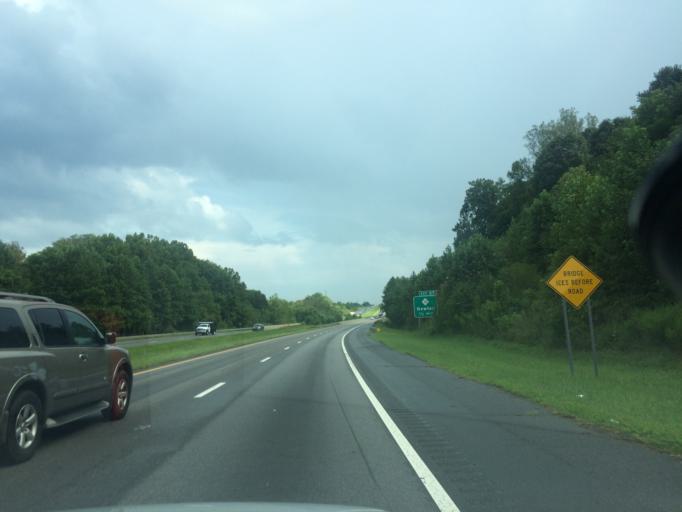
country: US
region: North Carolina
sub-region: Catawba County
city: Mountain View
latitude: 35.6453
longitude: -81.3055
